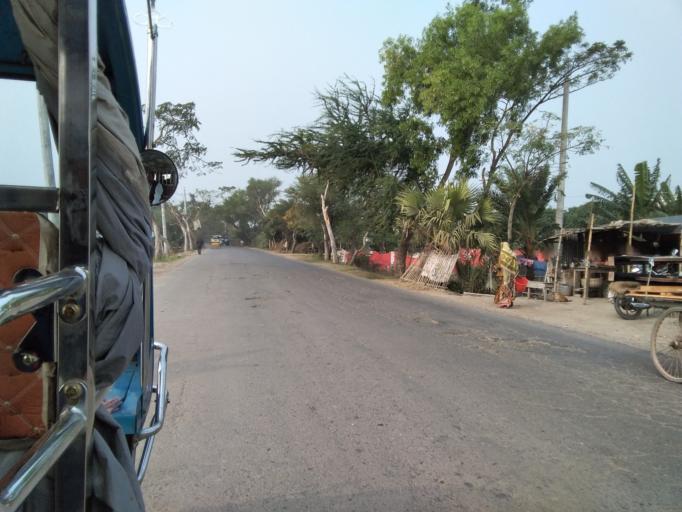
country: BD
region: Khulna
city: Satkhira
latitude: 22.6904
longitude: 89.0396
